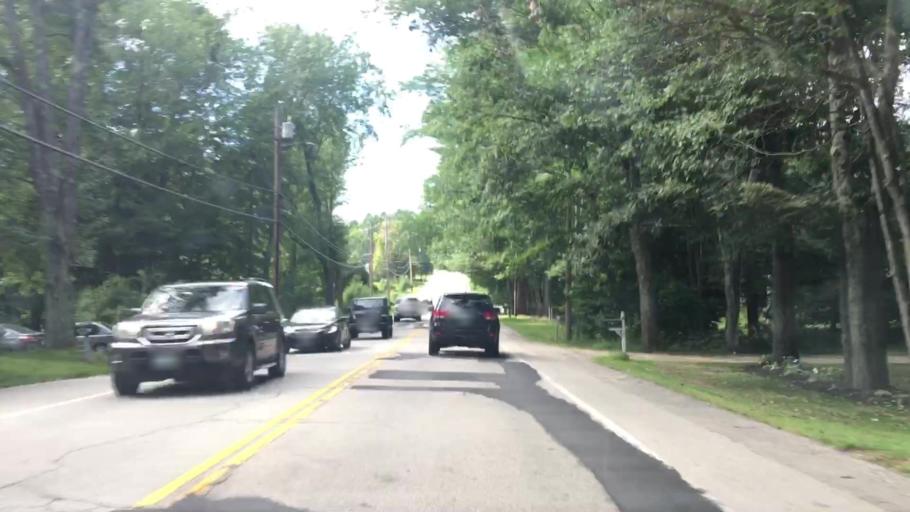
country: US
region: New Hampshire
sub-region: Strafford County
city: Somersworth
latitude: 43.2636
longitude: -70.9003
